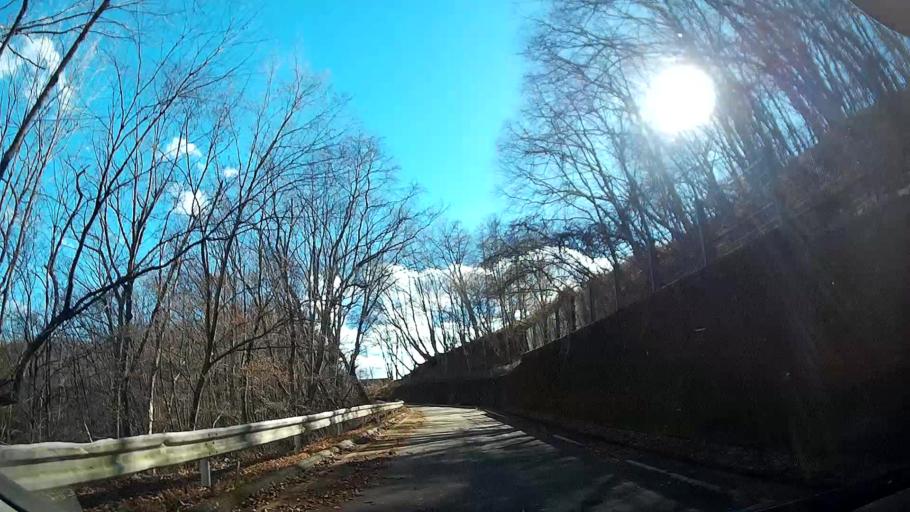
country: JP
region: Yamanashi
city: Otsuki
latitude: 35.7284
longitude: 138.9485
